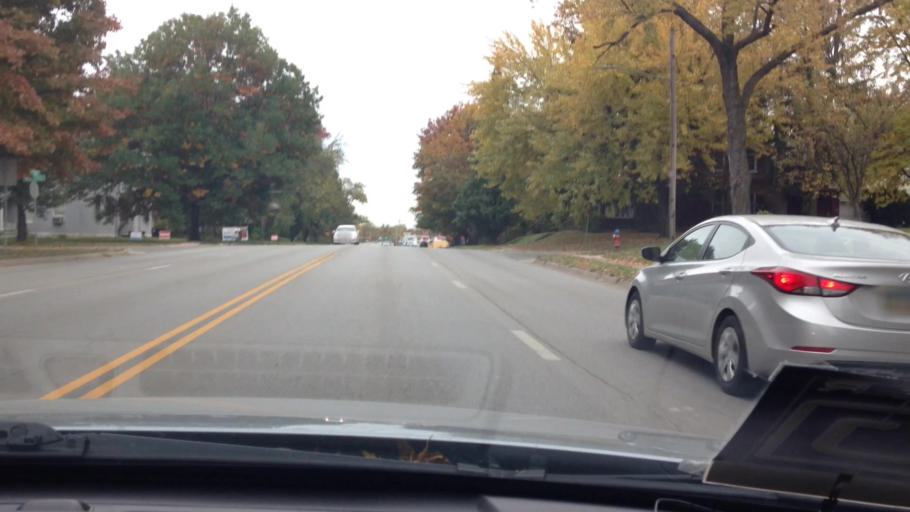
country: US
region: Kansas
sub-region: Leavenworth County
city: Leavenworth
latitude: 39.3090
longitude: -94.9115
